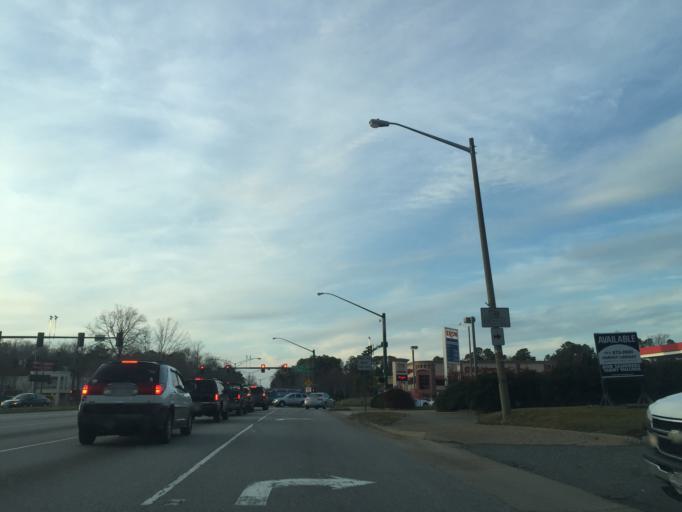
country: US
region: Virginia
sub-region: York County
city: Yorktown
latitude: 37.1034
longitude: -76.5116
